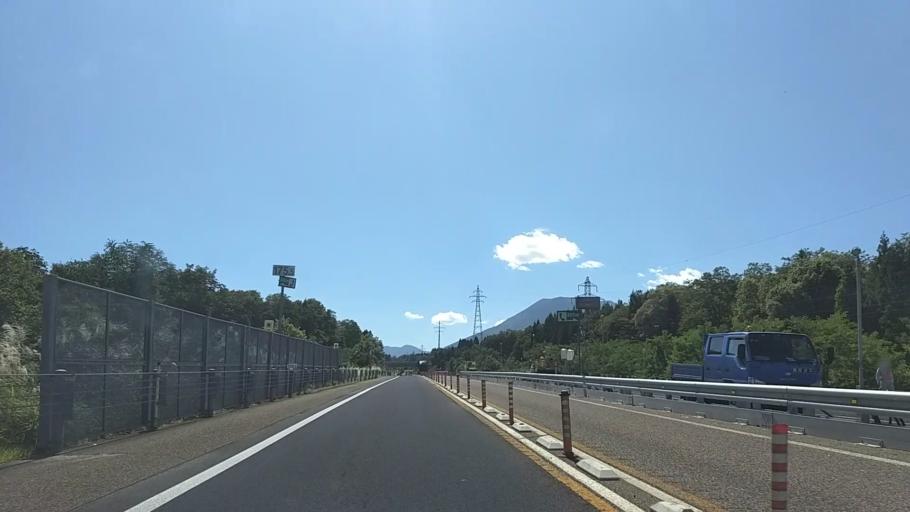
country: JP
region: Niigata
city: Arai
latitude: 36.8928
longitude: 138.2040
